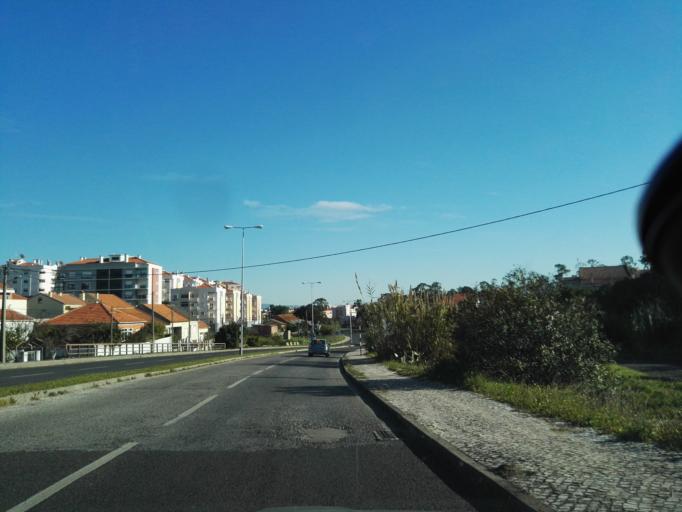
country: PT
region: Setubal
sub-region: Seixal
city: Corroios
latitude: 38.6468
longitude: -9.1582
